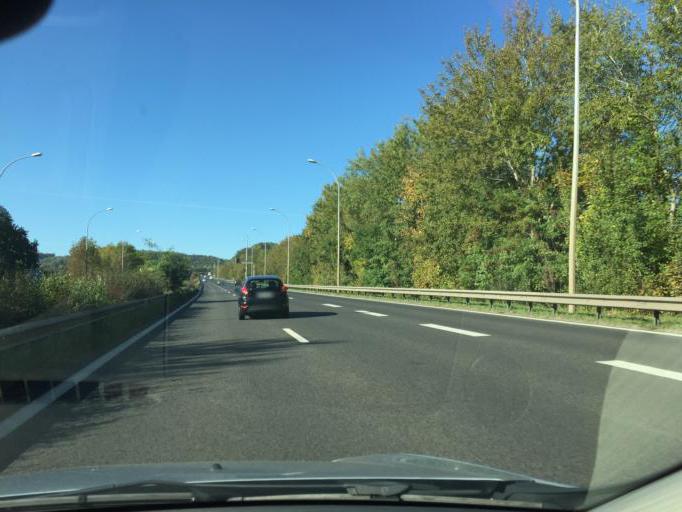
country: LU
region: Luxembourg
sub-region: Canton de Luxembourg
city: Niederanven
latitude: 49.6406
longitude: 6.2640
